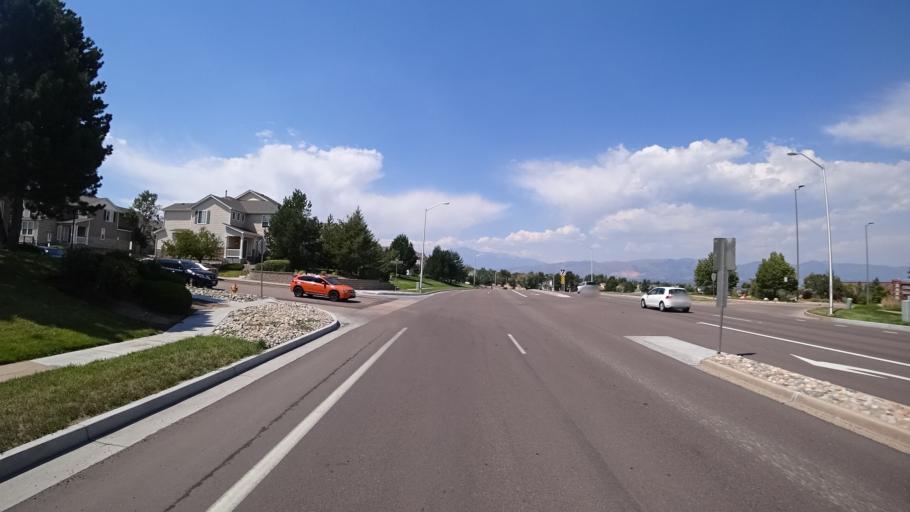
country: US
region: Colorado
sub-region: El Paso County
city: Cimarron Hills
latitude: 38.9264
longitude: -104.7538
